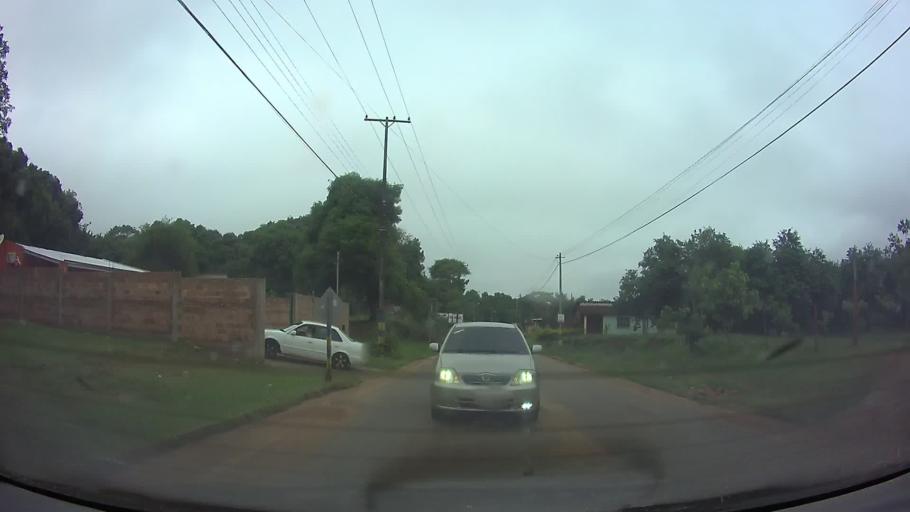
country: PY
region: Central
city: San Lorenzo
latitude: -25.3067
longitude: -57.4907
